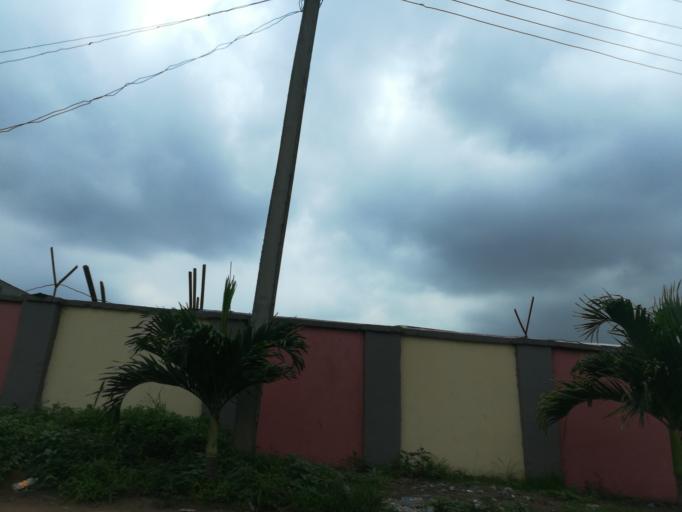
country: NG
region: Lagos
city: Agege
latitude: 6.6222
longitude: 3.3455
